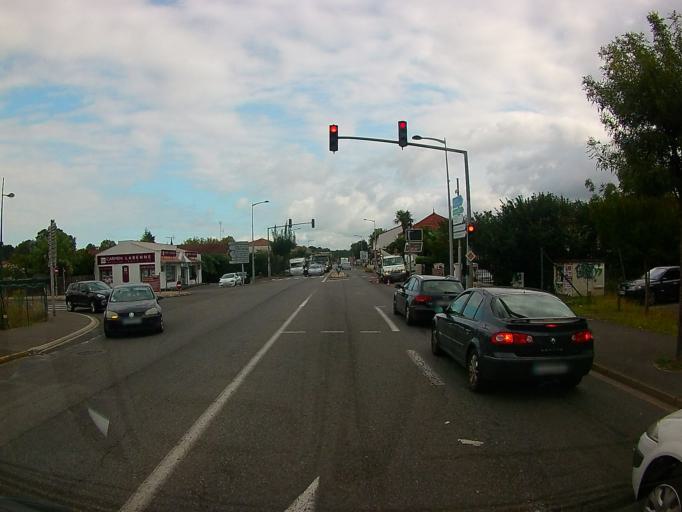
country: FR
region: Aquitaine
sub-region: Departement des Landes
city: Labenne
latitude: 43.5918
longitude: -1.4267
